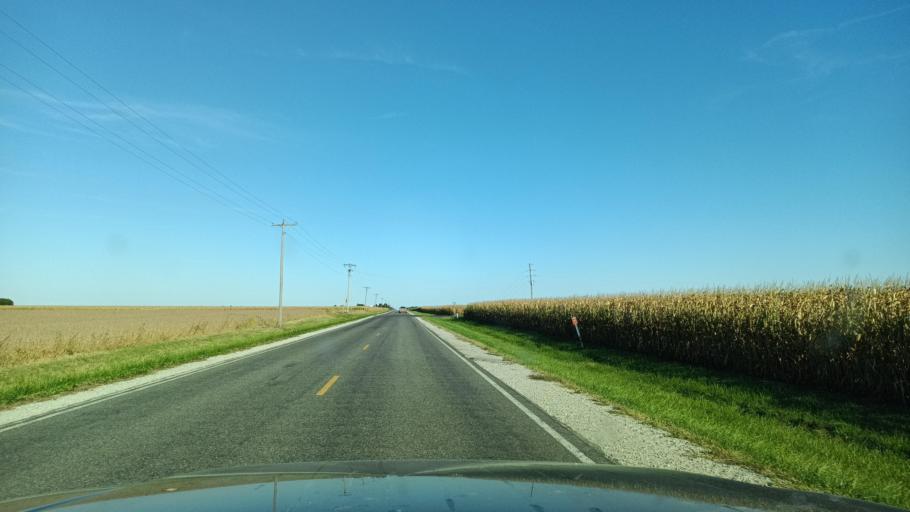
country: US
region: Illinois
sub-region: De Witt County
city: Clinton
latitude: 40.2245
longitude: -88.8603
